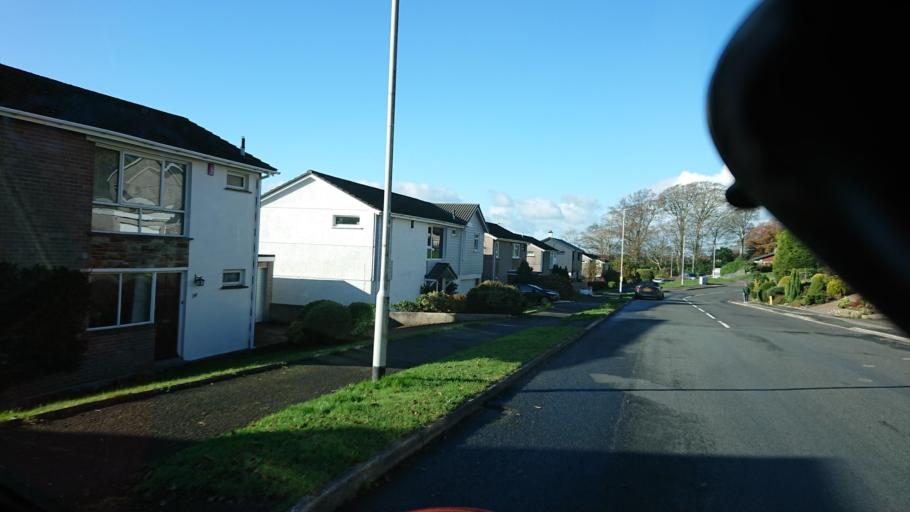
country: GB
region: England
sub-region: Plymouth
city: Plymouth
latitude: 50.4211
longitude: -4.1284
